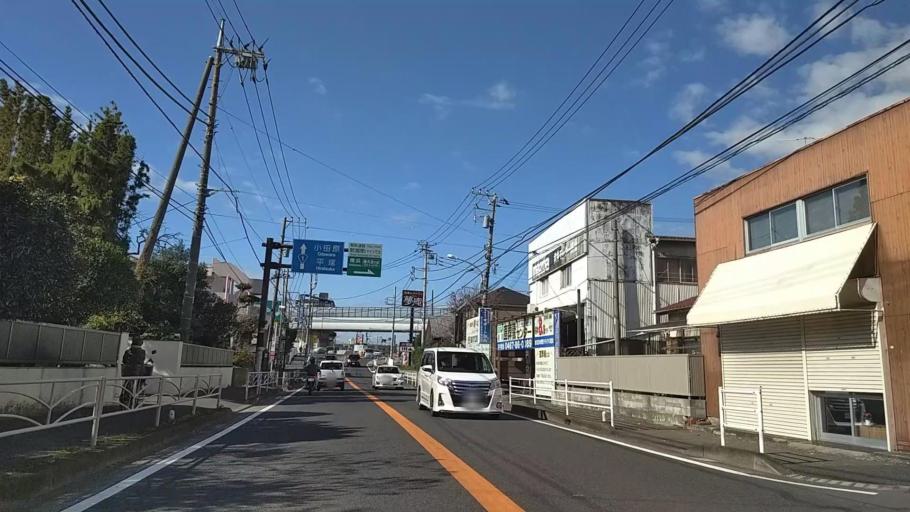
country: JP
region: Kanagawa
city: Chigasaki
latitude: 35.3327
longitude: 139.3862
